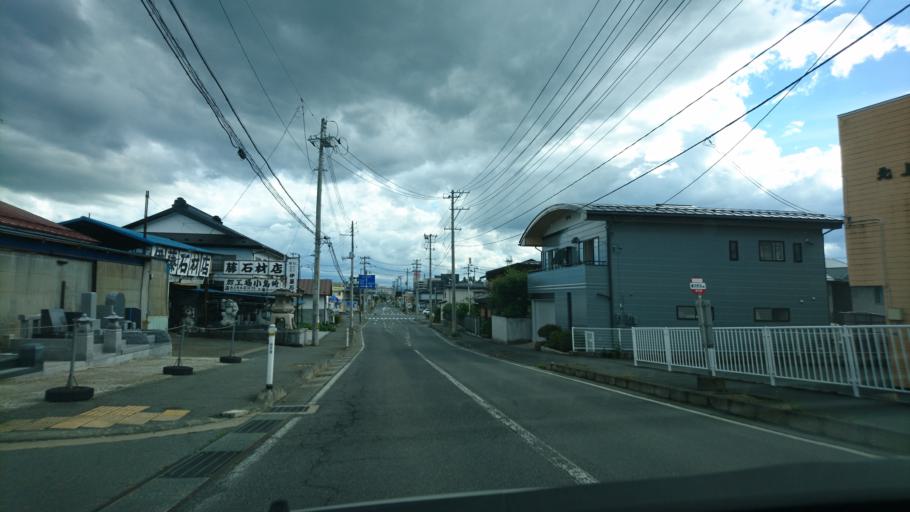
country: JP
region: Iwate
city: Kitakami
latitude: 39.2957
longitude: 141.1216
